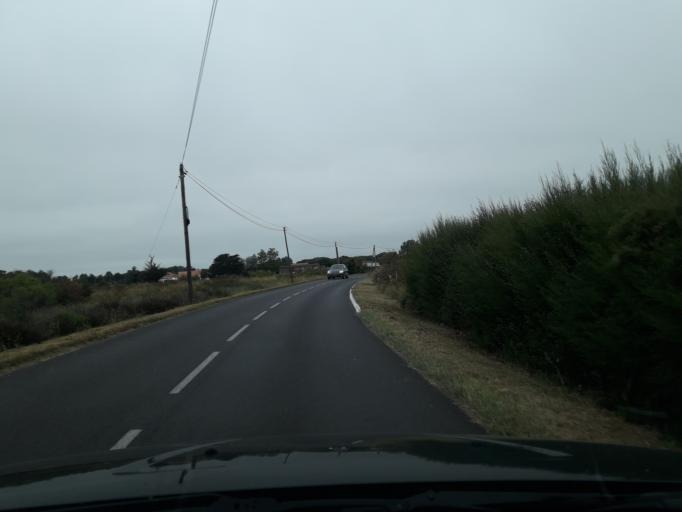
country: FR
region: Poitou-Charentes
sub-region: Departement de la Charente-Maritime
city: Boyard-Ville
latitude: 45.9553
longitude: -1.2487
